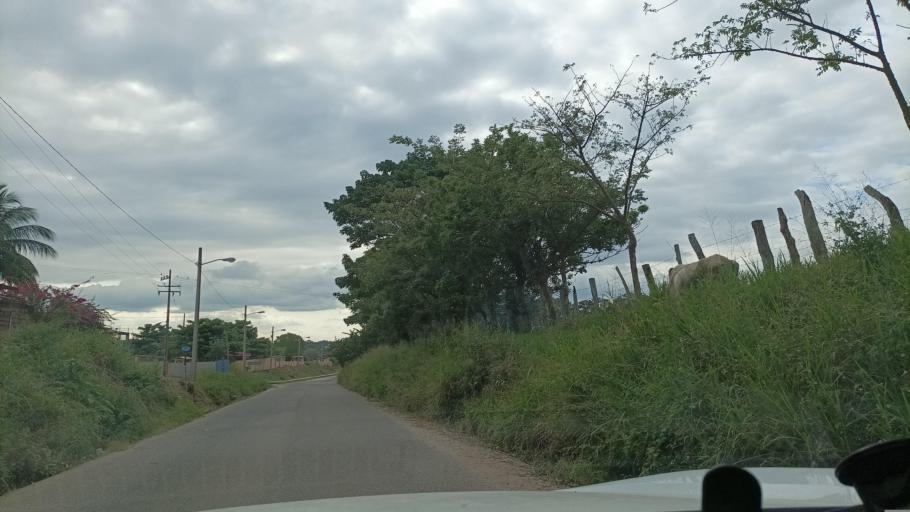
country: MX
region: Veracruz
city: Oluta
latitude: 17.9260
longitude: -94.8867
